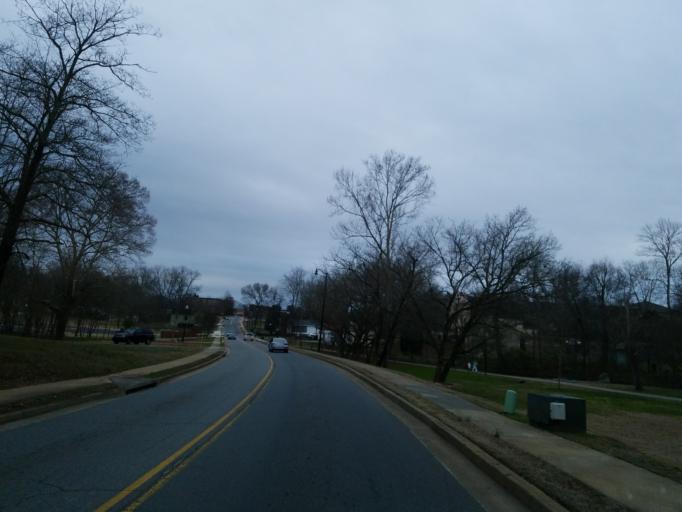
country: US
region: Georgia
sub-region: Cobb County
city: Acworth
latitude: 34.0702
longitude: -84.6768
